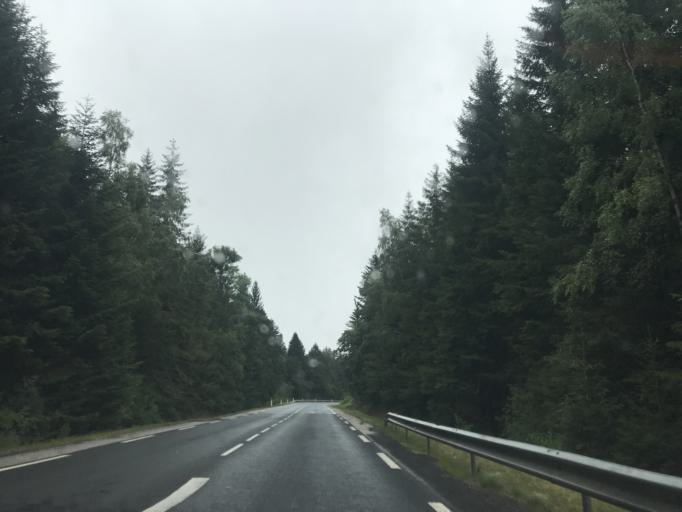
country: FR
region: Auvergne
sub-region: Departement de la Haute-Loire
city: Fontannes
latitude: 45.3416
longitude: 3.7113
